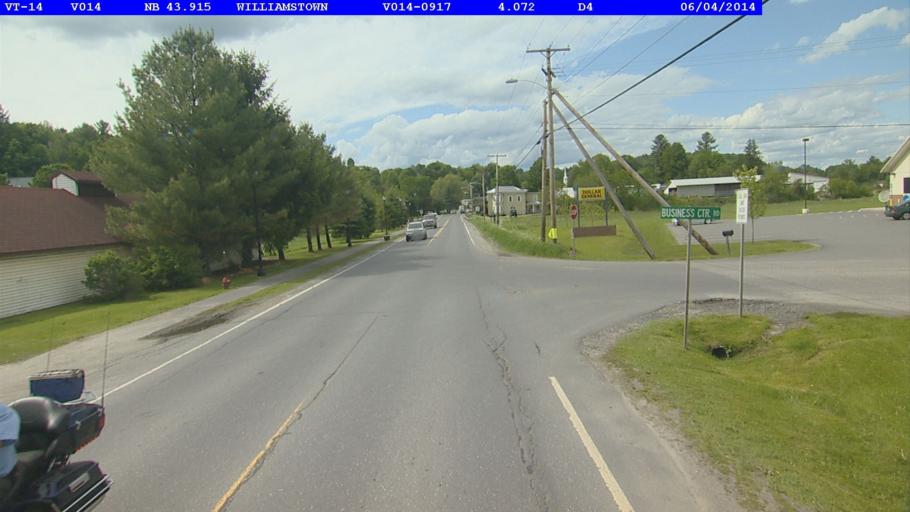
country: US
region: Vermont
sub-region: Orange County
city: Williamstown
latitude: 44.1164
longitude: -72.5402
